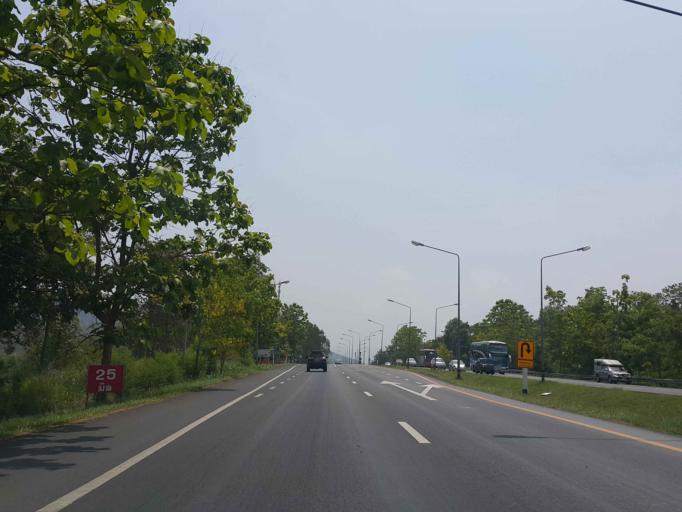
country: TH
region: Chiang Mai
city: San Sai
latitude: 18.8863
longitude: 99.1591
